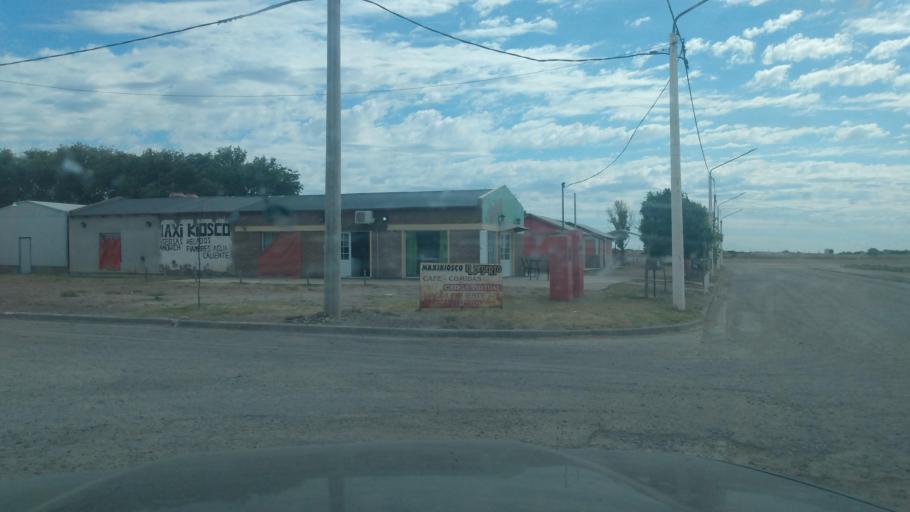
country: AR
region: La Pampa
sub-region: Departamento de Limay Mahuida
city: Limay Mahuida
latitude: -37.5516
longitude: -66.2242
